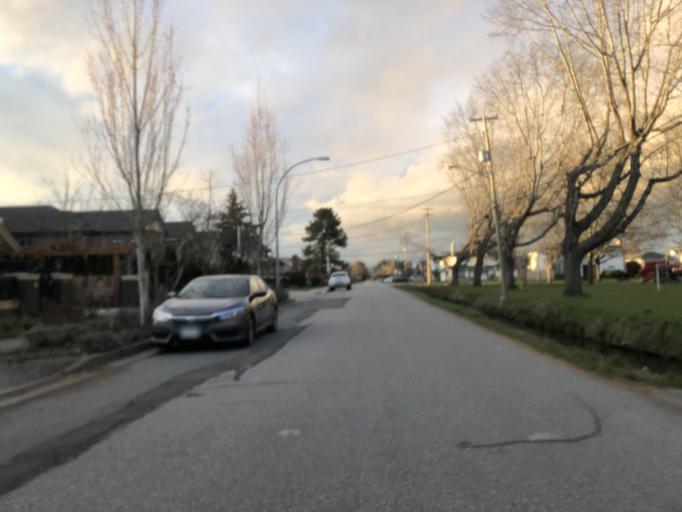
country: CA
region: British Columbia
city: Richmond
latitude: 49.1491
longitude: -123.1226
